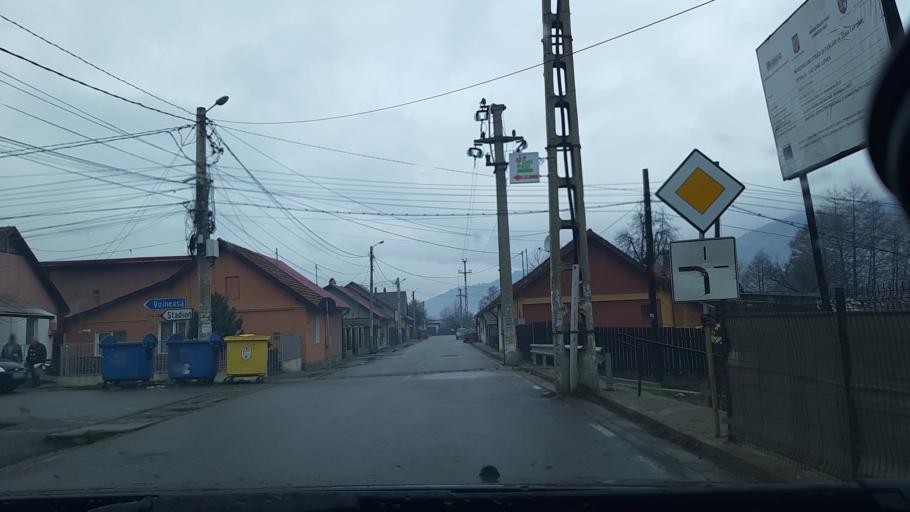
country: RO
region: Hunedoara
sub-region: Oras Petrila
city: Petrila
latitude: 45.4459
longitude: 23.4125
